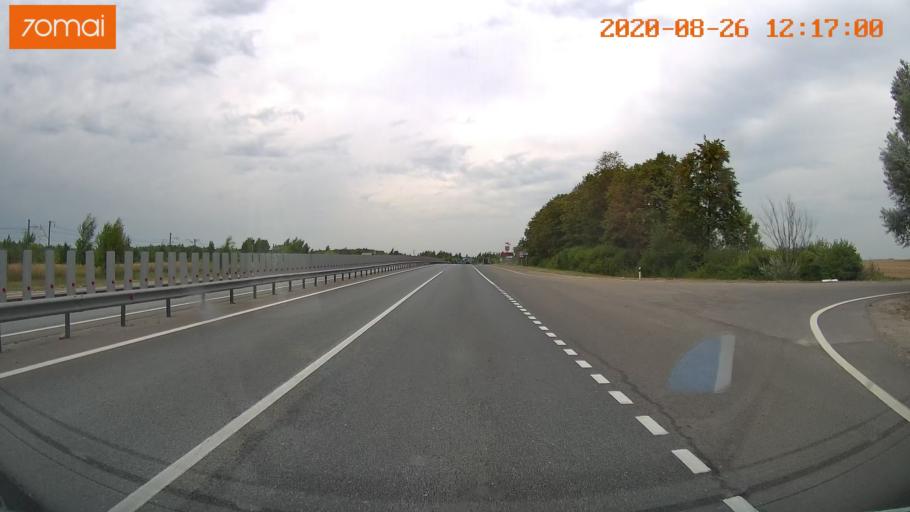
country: RU
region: Rjazan
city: Murmino
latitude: 54.4546
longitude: 40.0335
